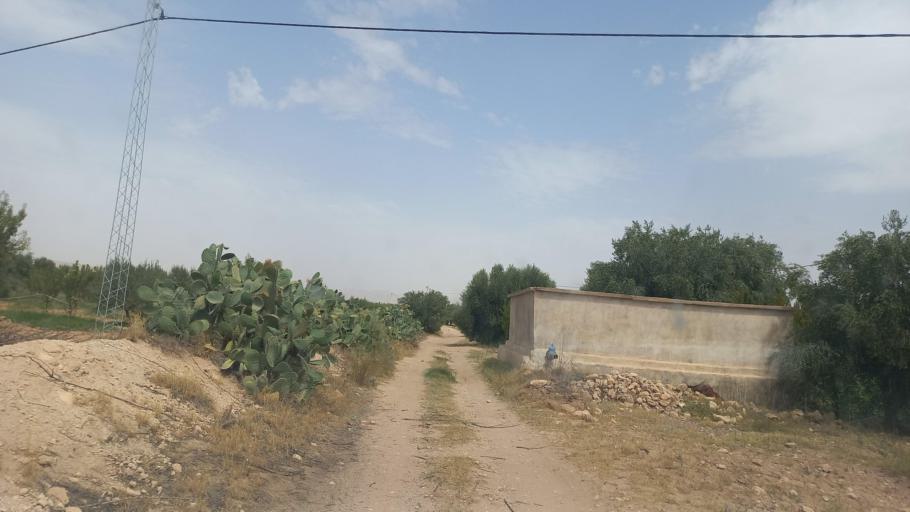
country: TN
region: Al Qasrayn
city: Kasserine
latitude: 35.2606
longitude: 9.0000
